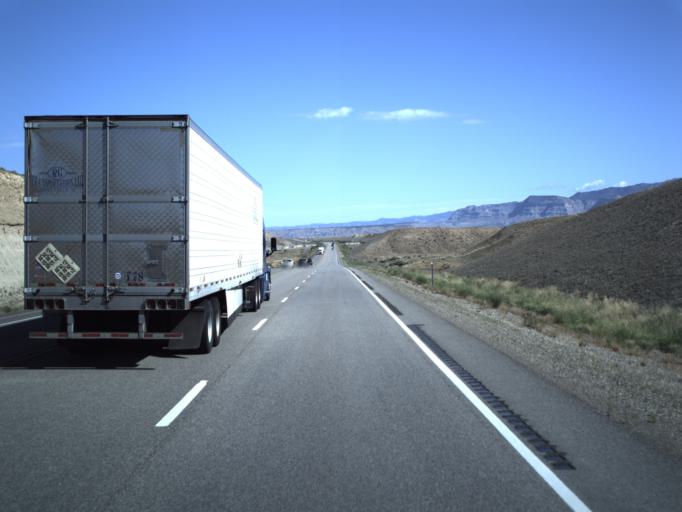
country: US
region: Utah
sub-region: Carbon County
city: East Carbon City
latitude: 39.2802
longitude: -110.3490
